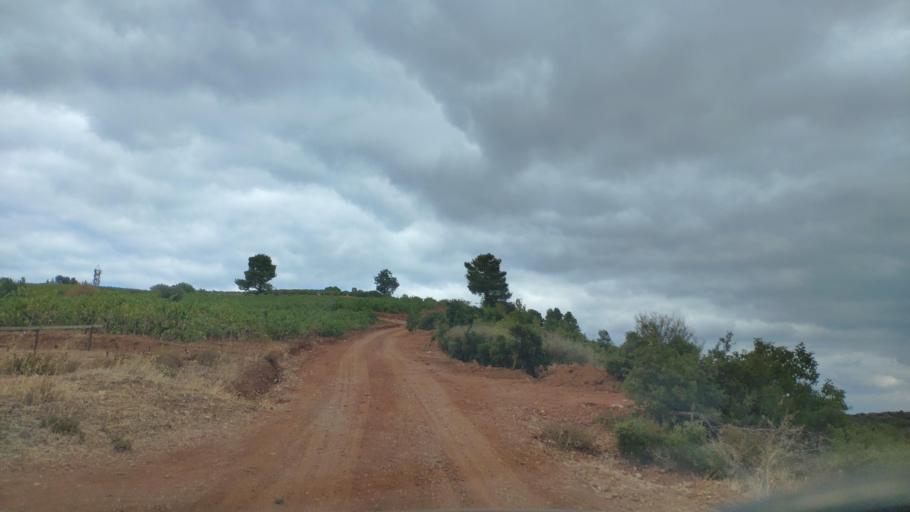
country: GR
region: West Greece
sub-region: Nomos Achaias
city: Temeni
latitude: 38.1769
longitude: 22.1589
